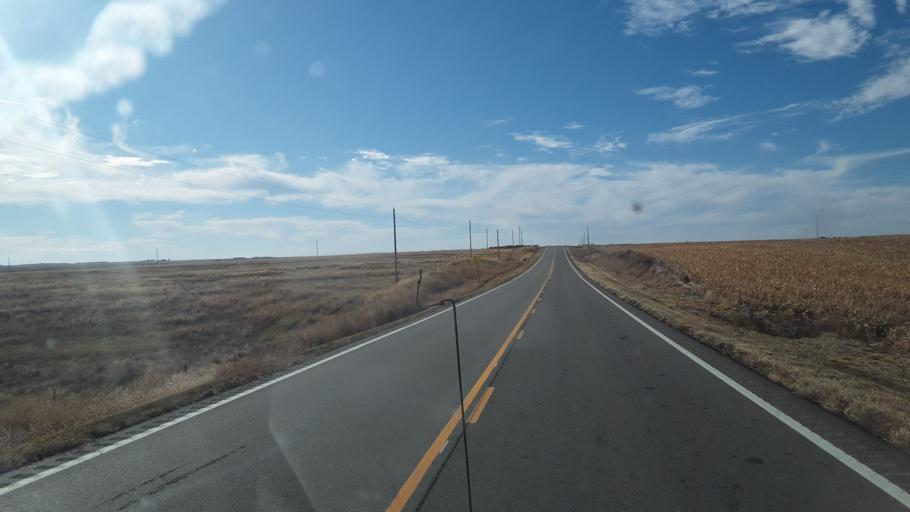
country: US
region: Kansas
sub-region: Hodgeman County
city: Jetmore
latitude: 38.0726
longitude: -100.0777
